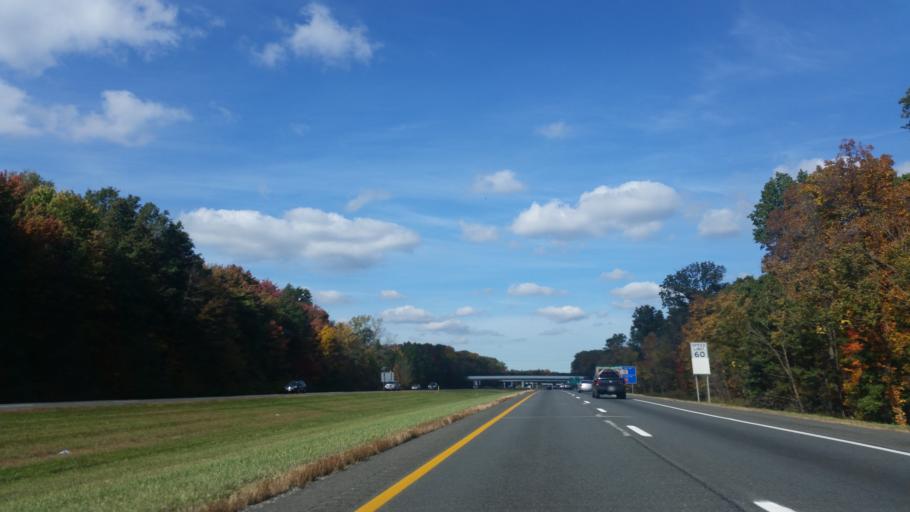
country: US
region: Ohio
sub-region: Cuyahoga County
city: Brecksville
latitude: 41.2963
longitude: -81.6407
